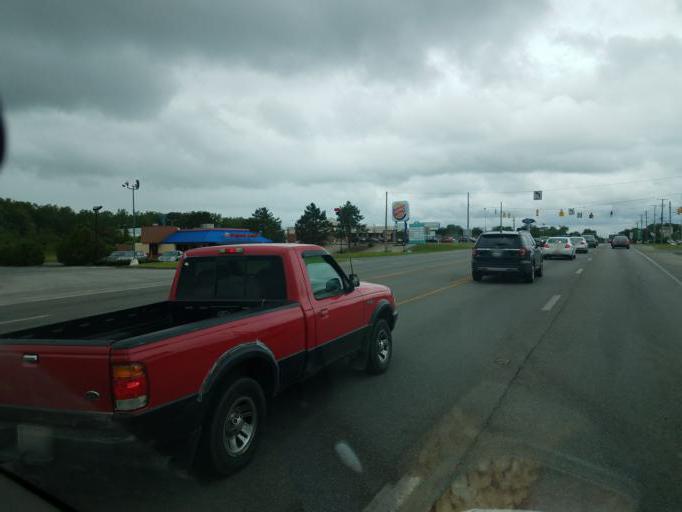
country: US
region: Ohio
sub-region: Marion County
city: Marion
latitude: 40.5663
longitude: -83.1208
